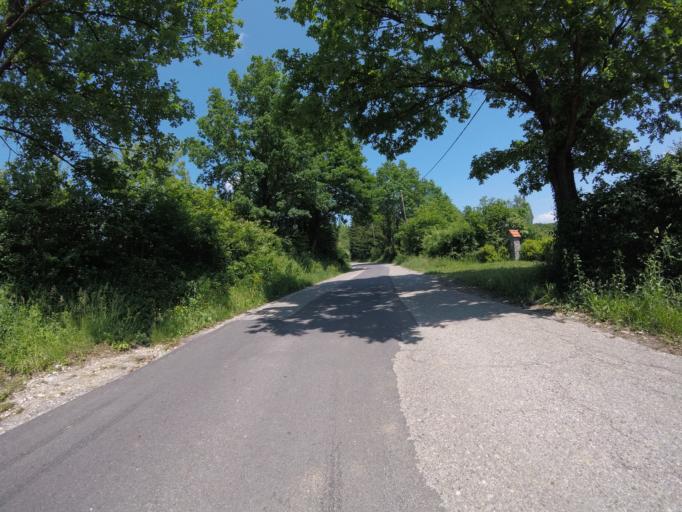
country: HR
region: Grad Zagreb
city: Strmec
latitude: 45.5707
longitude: 15.9468
